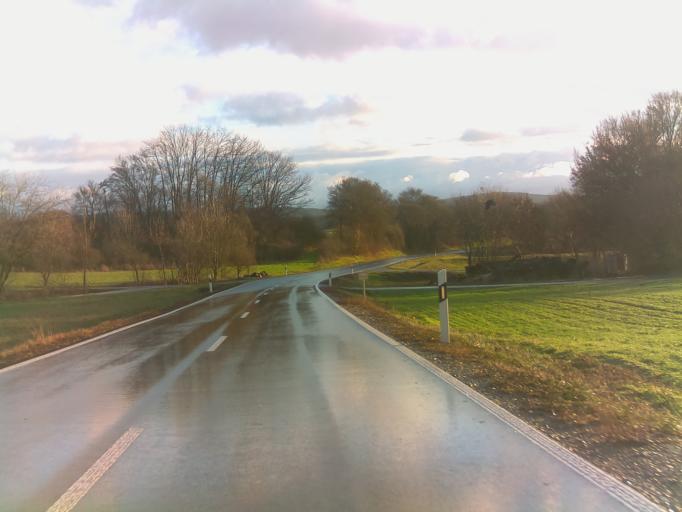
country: DE
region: Bavaria
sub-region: Regierungsbezirk Unterfranken
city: Hausen
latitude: 50.4912
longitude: 10.1324
